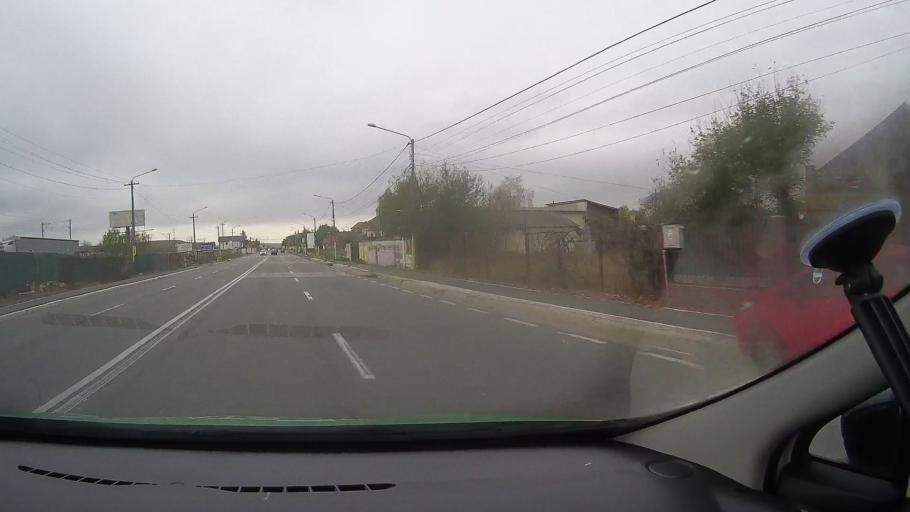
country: RO
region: Constanta
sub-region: Comuna Valu lui Traian
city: Valu lui Traian
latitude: 44.1688
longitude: 28.4447
